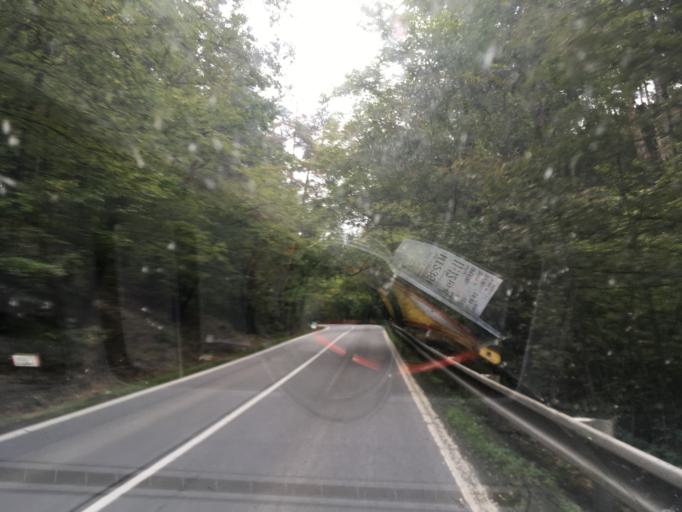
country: CZ
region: Vysocina
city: Namest' nad Oslavou
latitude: 49.1966
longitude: 16.2237
